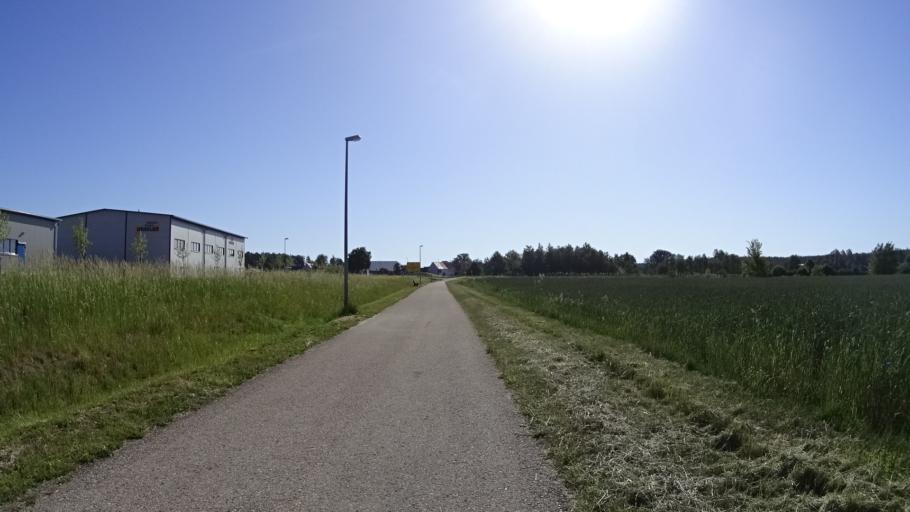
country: DE
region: Bavaria
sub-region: Regierungsbezirk Mittelfranken
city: Arberg
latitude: 49.1601
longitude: 10.5681
